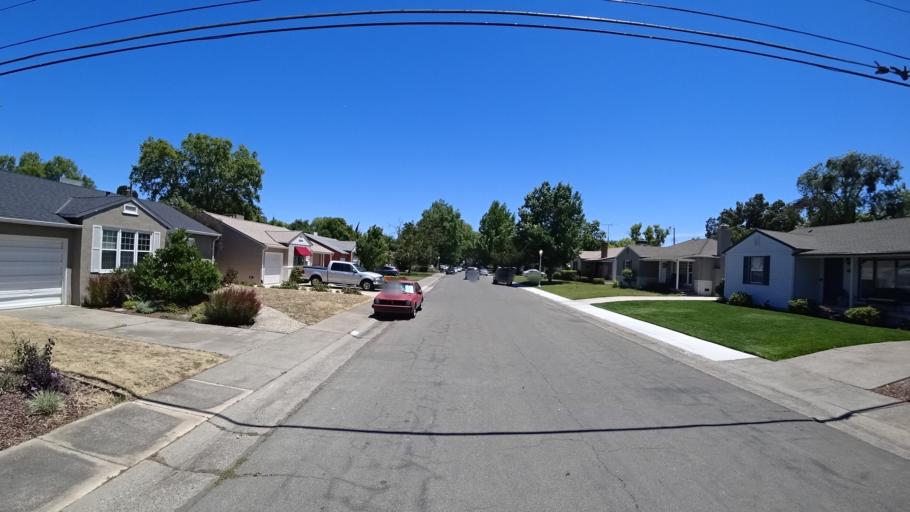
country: US
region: California
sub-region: Sacramento County
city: Sacramento
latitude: 38.5764
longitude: -121.4398
